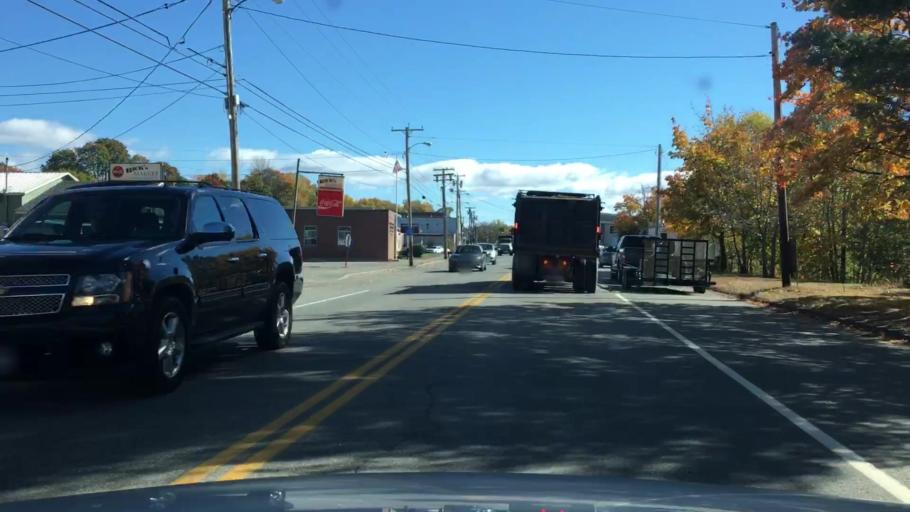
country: US
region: Maine
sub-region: Penobscot County
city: East Millinocket
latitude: 45.6264
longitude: -68.5789
